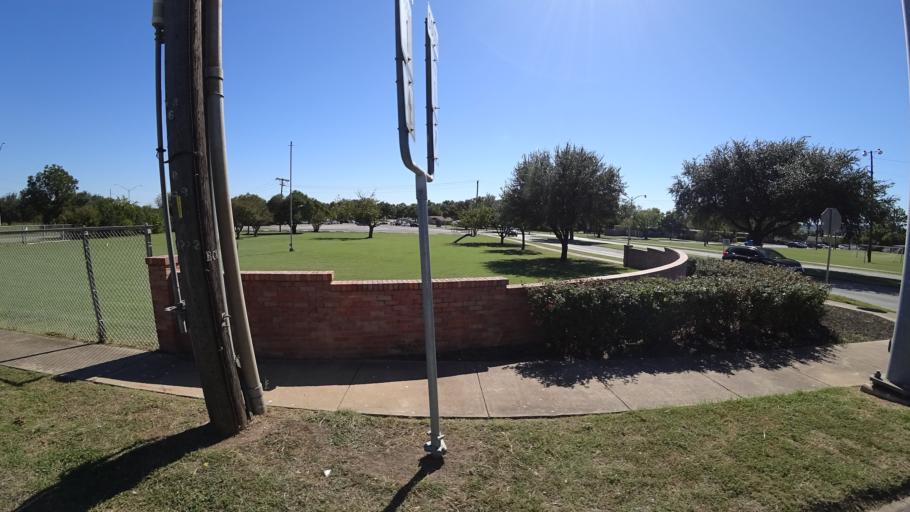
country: US
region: Texas
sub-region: Travis County
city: West Lake Hills
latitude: 30.3094
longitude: -97.7597
